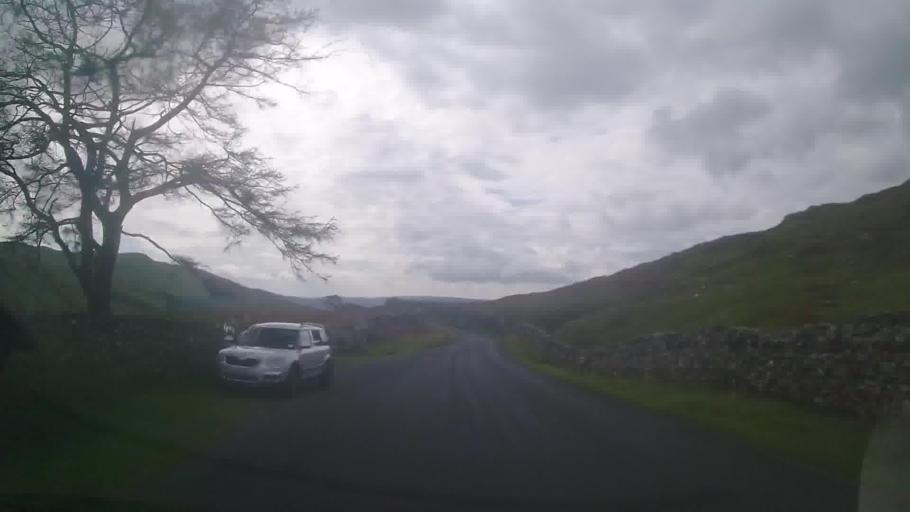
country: GB
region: England
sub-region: Cumbria
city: Ambleside
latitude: 54.4510
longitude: -2.9381
